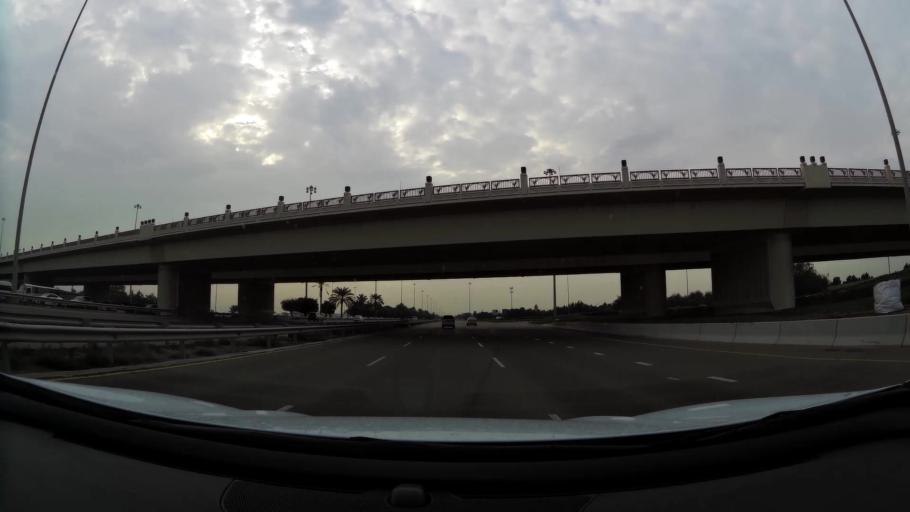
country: AE
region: Abu Dhabi
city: Abu Dhabi
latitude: 24.3755
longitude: 54.5515
